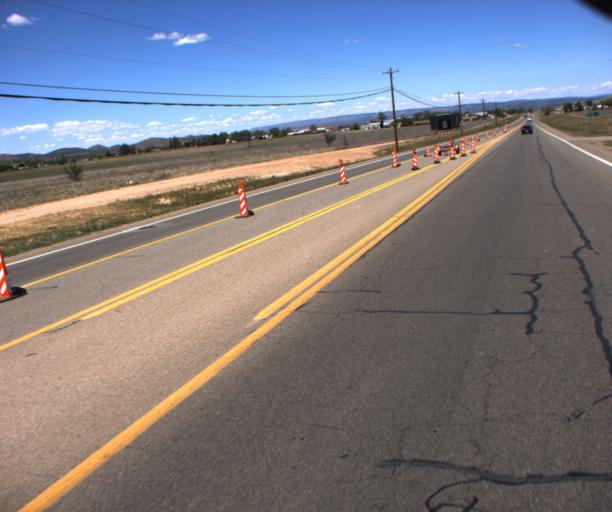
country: US
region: Arizona
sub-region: Yavapai County
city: Chino Valley
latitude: 34.7767
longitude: -112.4527
